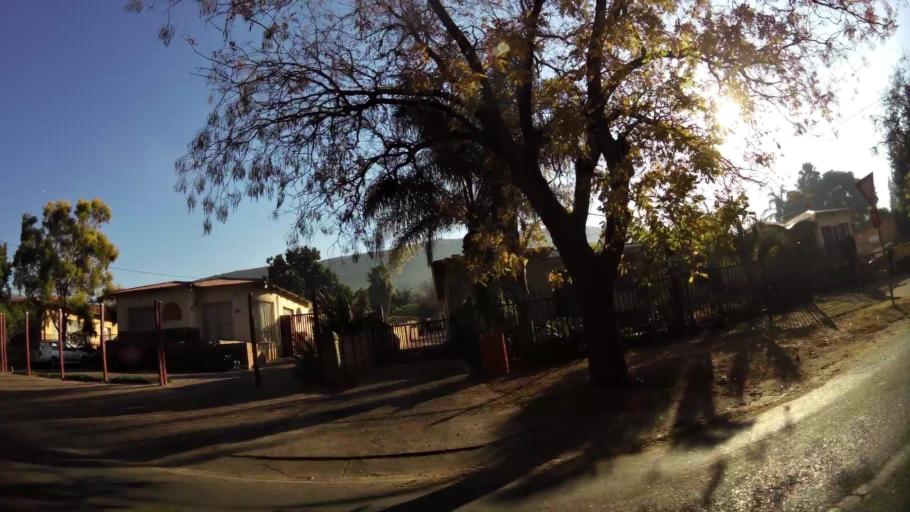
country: ZA
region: Gauteng
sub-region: City of Tshwane Metropolitan Municipality
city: Pretoria
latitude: -25.6986
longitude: 28.1668
